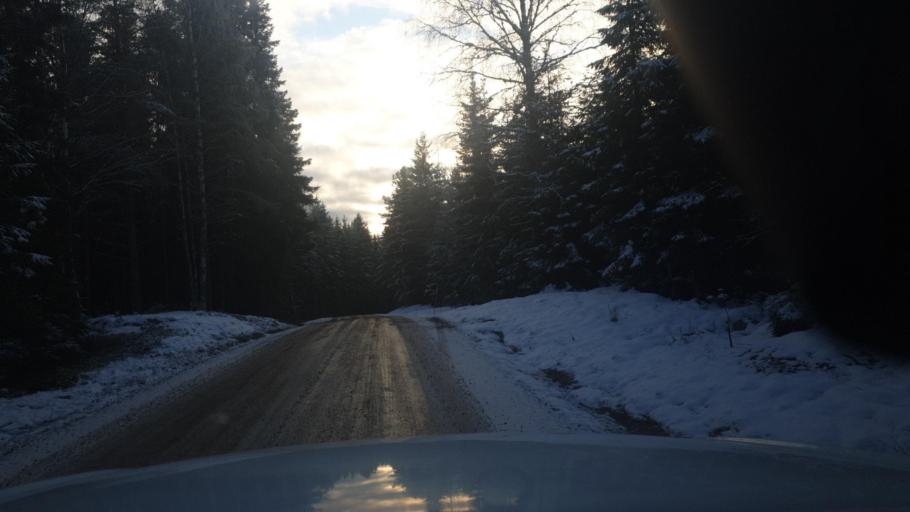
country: SE
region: Vaermland
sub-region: Arvika Kommun
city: Arvika
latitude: 59.9689
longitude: 12.6602
